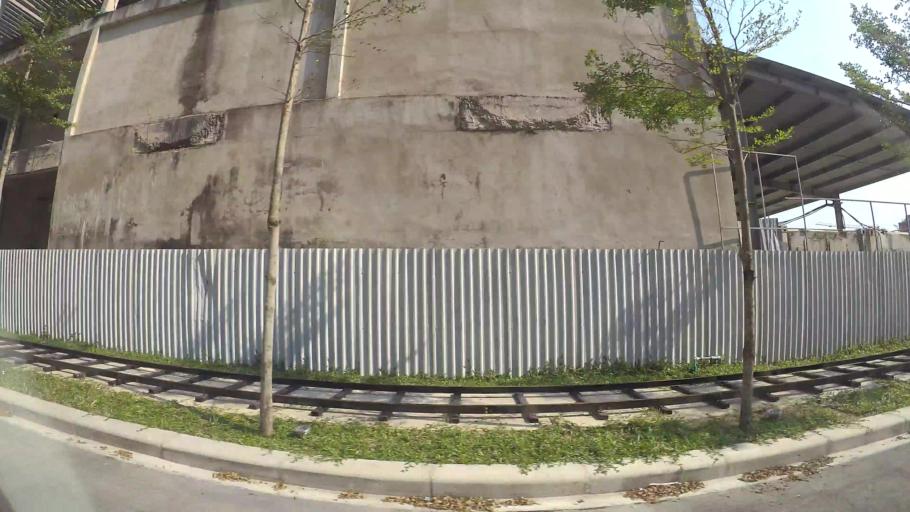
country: VN
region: Da Nang
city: Ngu Hanh Son
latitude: 15.9658
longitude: 108.2821
